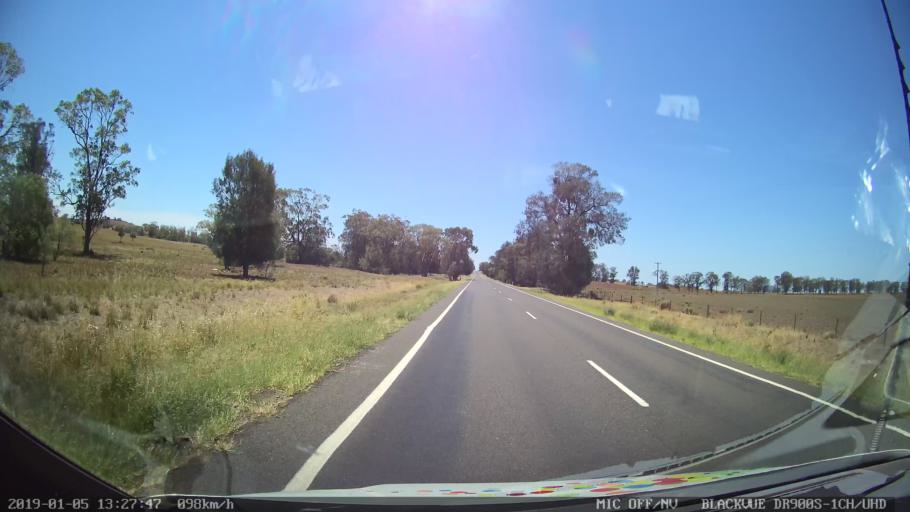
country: AU
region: New South Wales
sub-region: Gunnedah
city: Gunnedah
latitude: -31.0415
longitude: 150.0342
